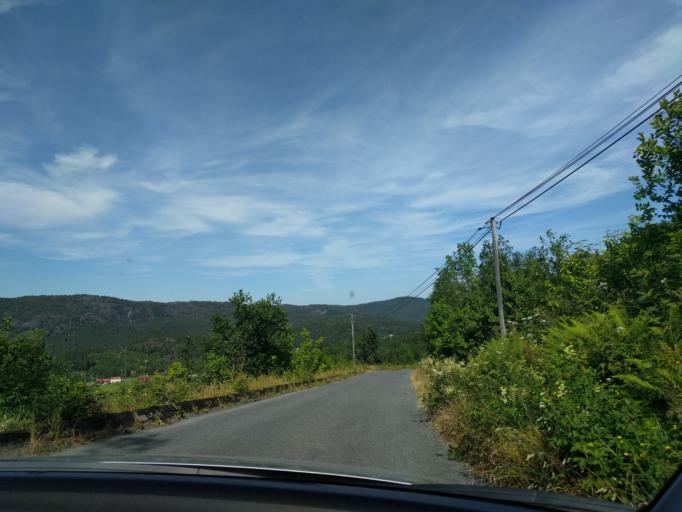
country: NO
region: Aust-Agder
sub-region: Gjerstad
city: Gjerstad
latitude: 58.8889
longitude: 8.9614
